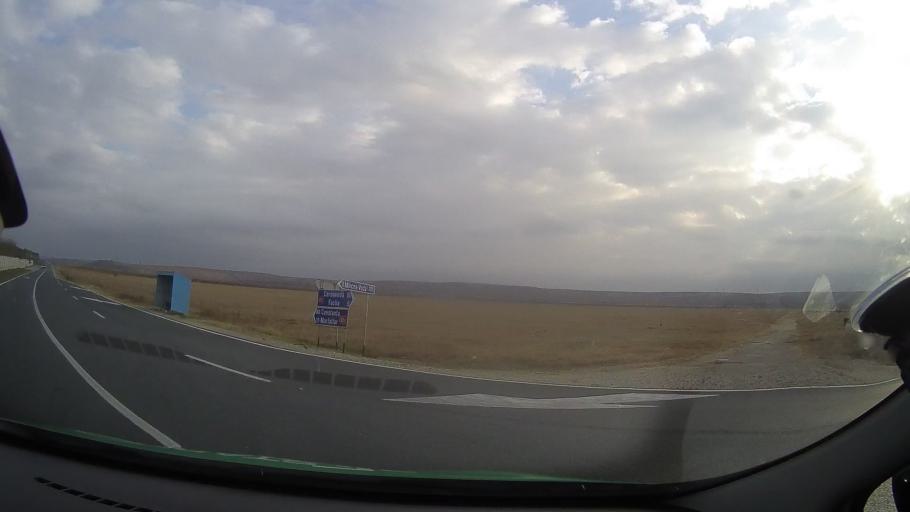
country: RO
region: Constanta
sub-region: Comuna Mircea Voda
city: Mircea Voda
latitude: 44.2712
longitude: 28.1722
